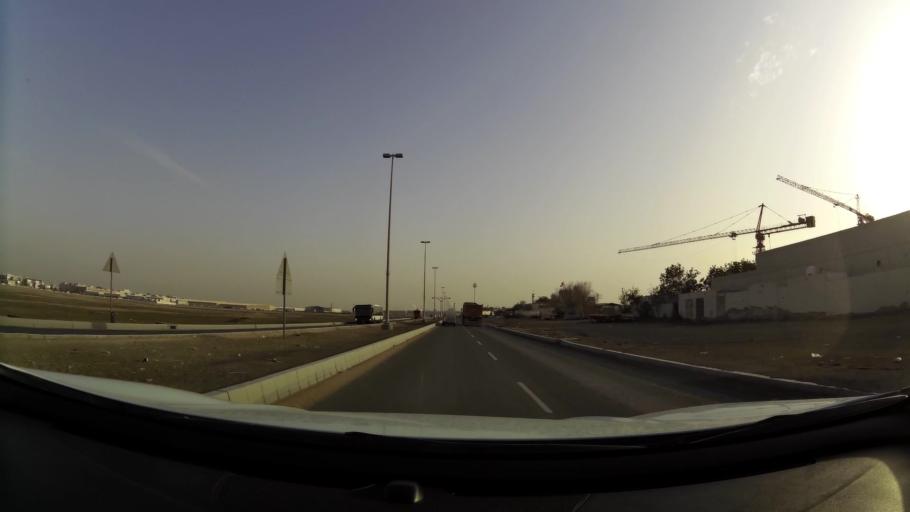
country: AE
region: Abu Dhabi
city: Abu Dhabi
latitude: 24.3435
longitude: 54.5124
